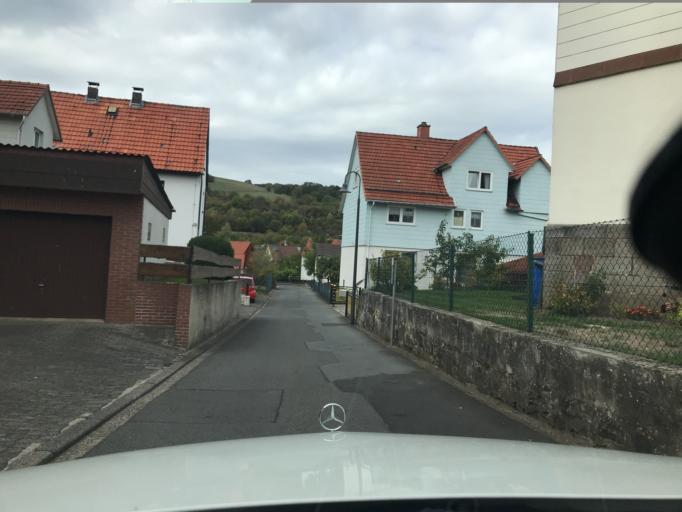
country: DE
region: Hesse
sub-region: Regierungsbezirk Kassel
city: Grossalmerode
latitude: 51.2326
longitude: 9.8135
